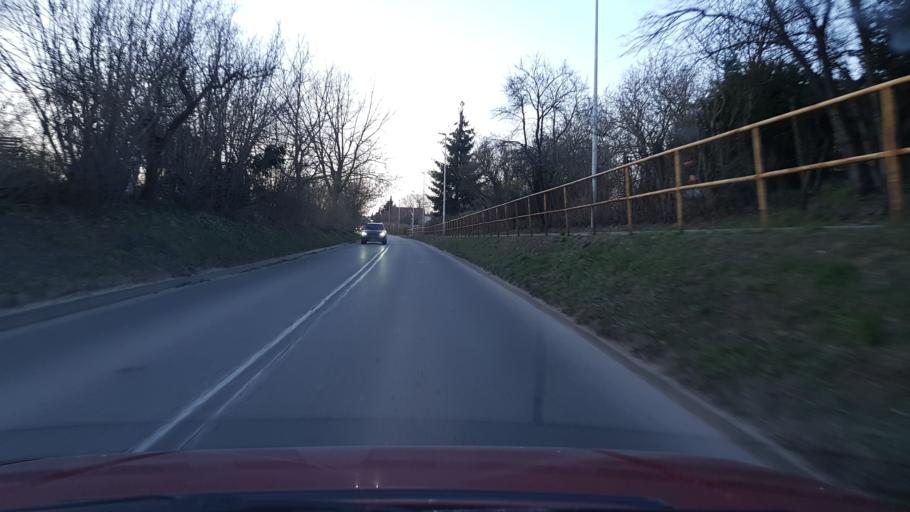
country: PL
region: West Pomeranian Voivodeship
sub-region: Szczecin
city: Szczecin
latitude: 53.4642
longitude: 14.5539
